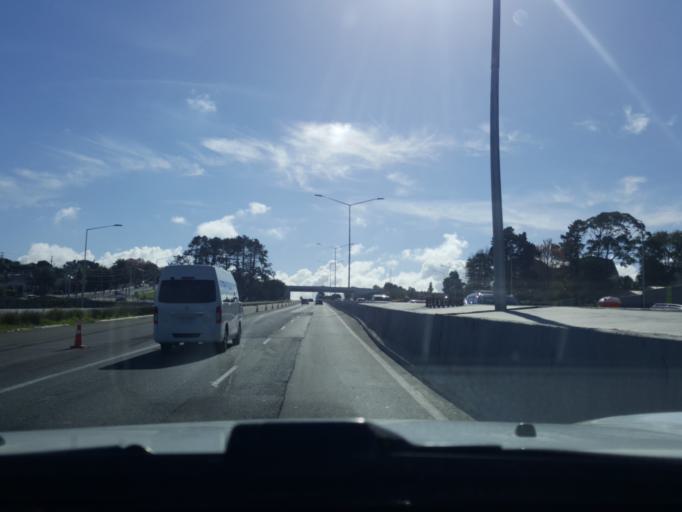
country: NZ
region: Auckland
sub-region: Auckland
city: Rosebank
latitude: -36.8358
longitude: 174.6199
